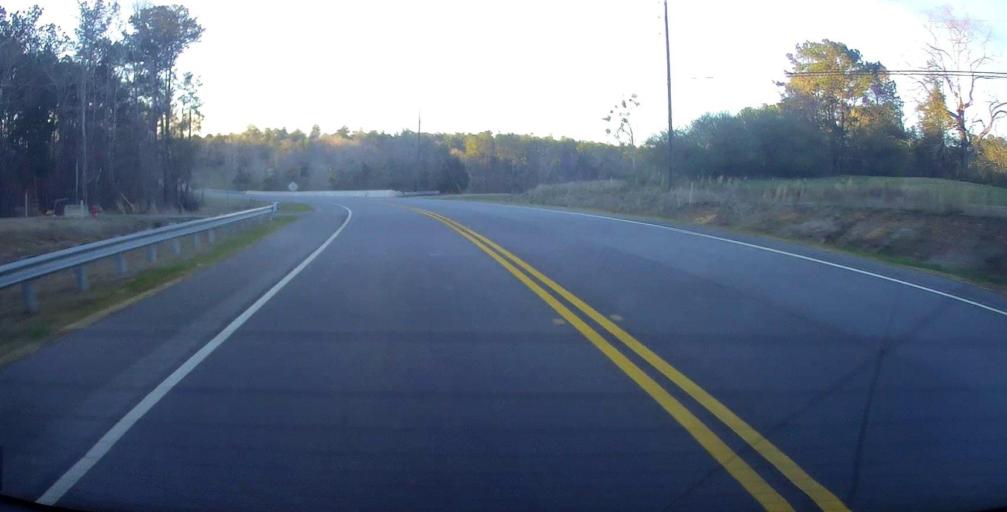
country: US
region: Alabama
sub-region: Lee County
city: Smiths Station
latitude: 32.6161
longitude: -85.0268
